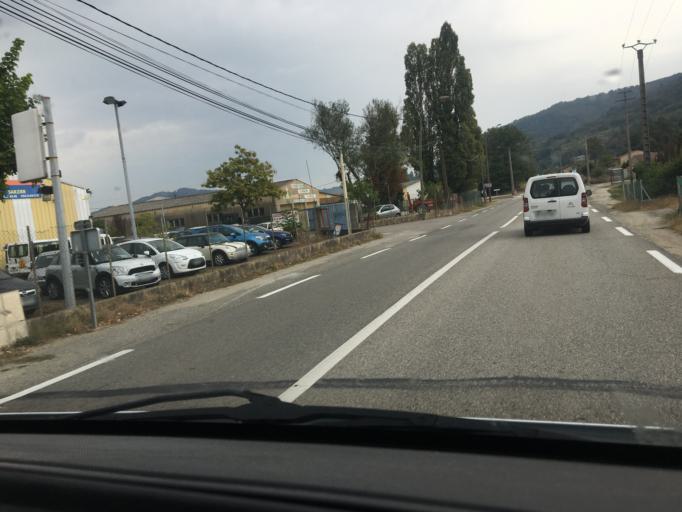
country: FR
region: Rhone-Alpes
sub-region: Departement de l'Ardeche
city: Saint-Jean-de-Muzols
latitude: 45.0669
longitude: 4.8008
